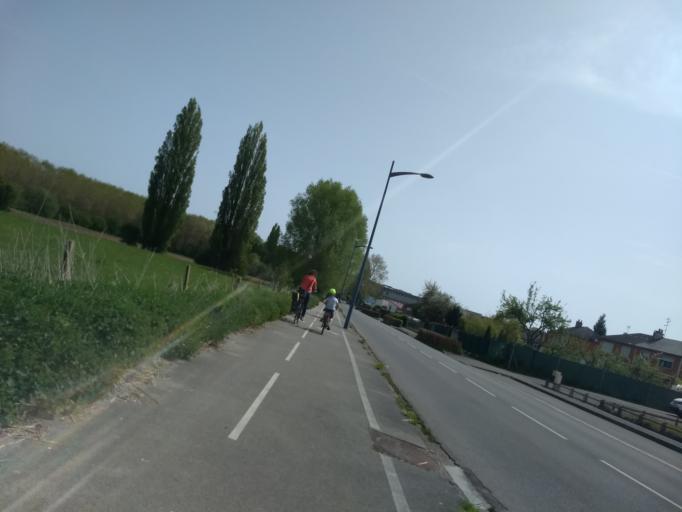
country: FR
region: Nord-Pas-de-Calais
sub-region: Departement du Pas-de-Calais
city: Anzin-Saint-Aubin
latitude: 50.3041
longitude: 2.7488
